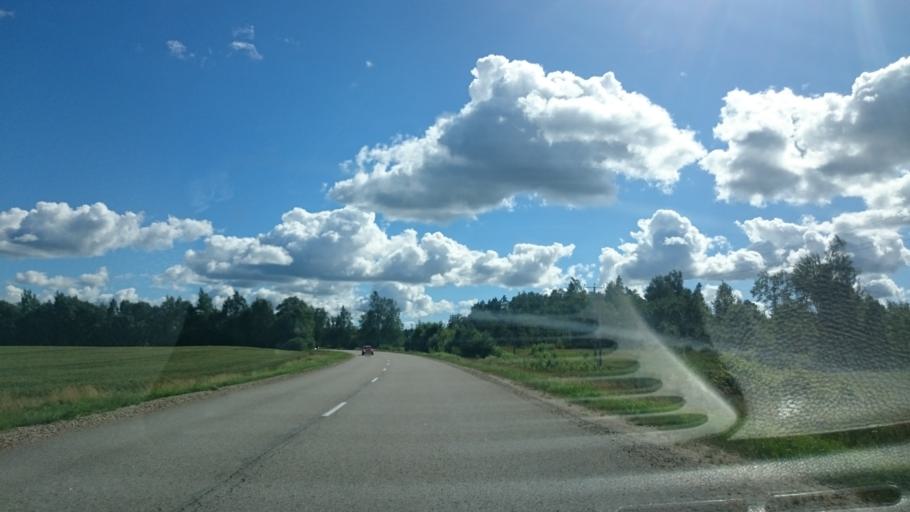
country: LV
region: Kuldigas Rajons
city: Kuldiga
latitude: 56.9007
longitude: 21.8905
